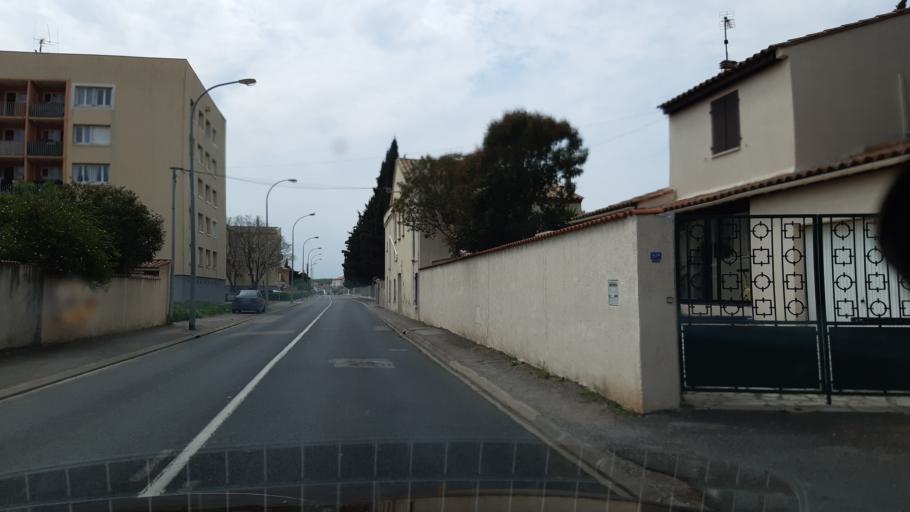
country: FR
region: Languedoc-Roussillon
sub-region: Departement de l'Aude
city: Narbonne
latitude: 43.1895
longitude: 3.0238
